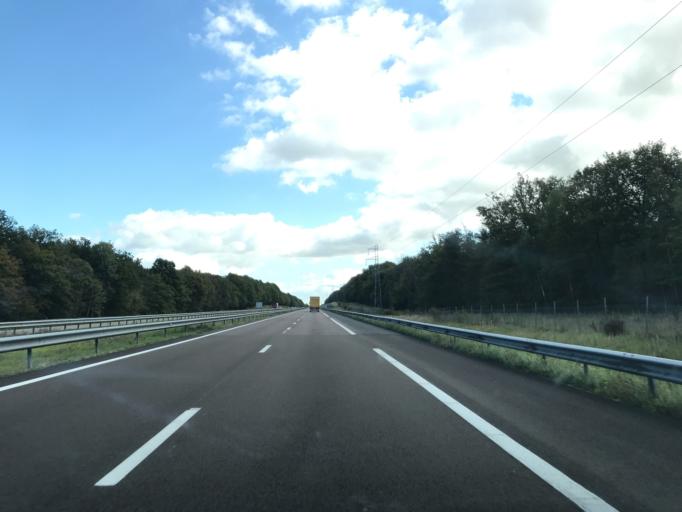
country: FR
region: Centre
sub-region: Departement du Loiret
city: Courtenay
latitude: 48.0799
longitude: 3.0545
